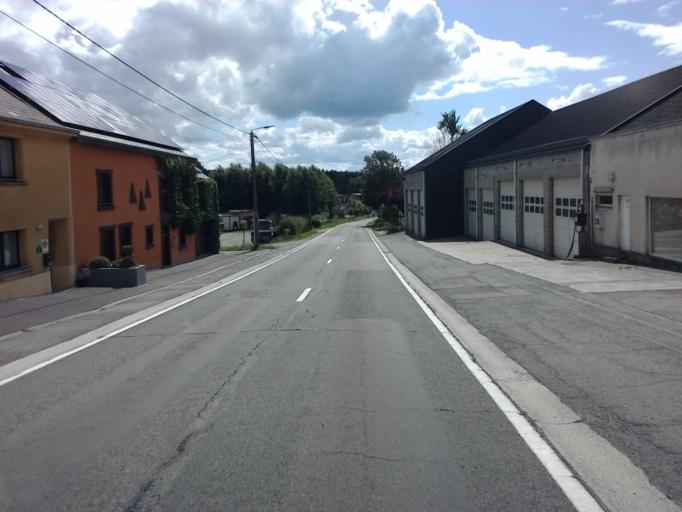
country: BE
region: Wallonia
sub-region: Province du Luxembourg
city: Habay-la-Vieille
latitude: 49.7837
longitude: 5.6053
